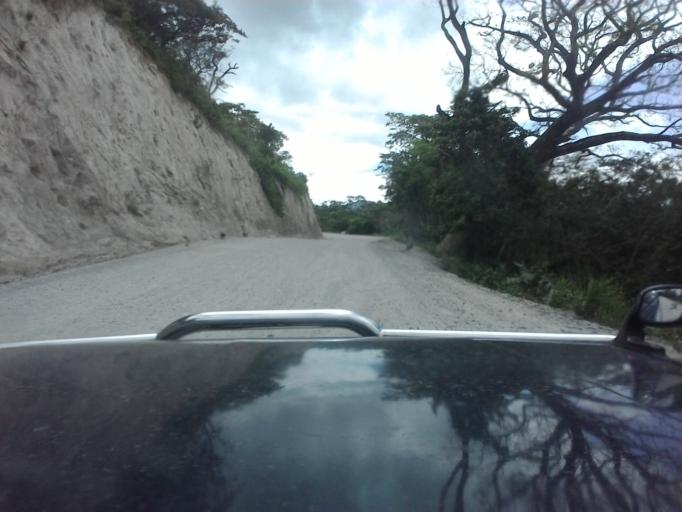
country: CR
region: Guanacaste
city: Juntas
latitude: 10.2397
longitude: -84.8495
